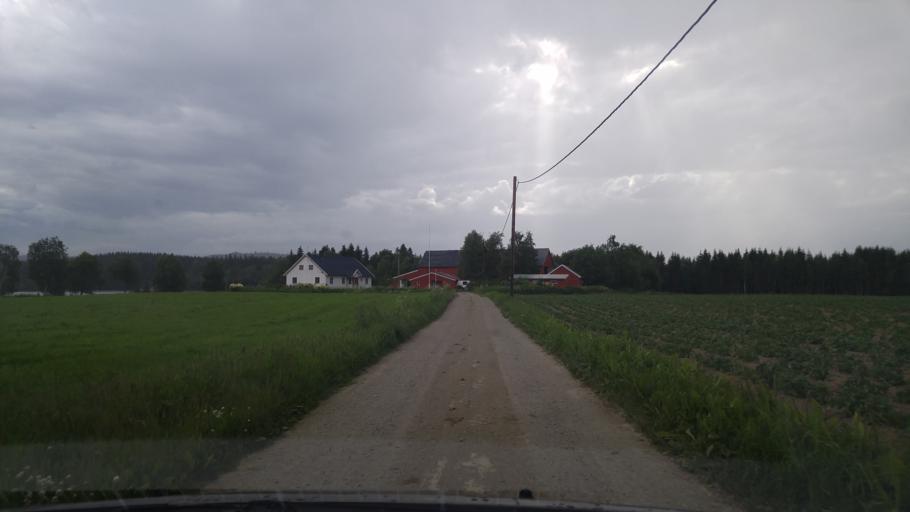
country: NO
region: Nord-Trondelag
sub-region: Levanger
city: Skogn
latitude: 63.6275
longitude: 11.2593
